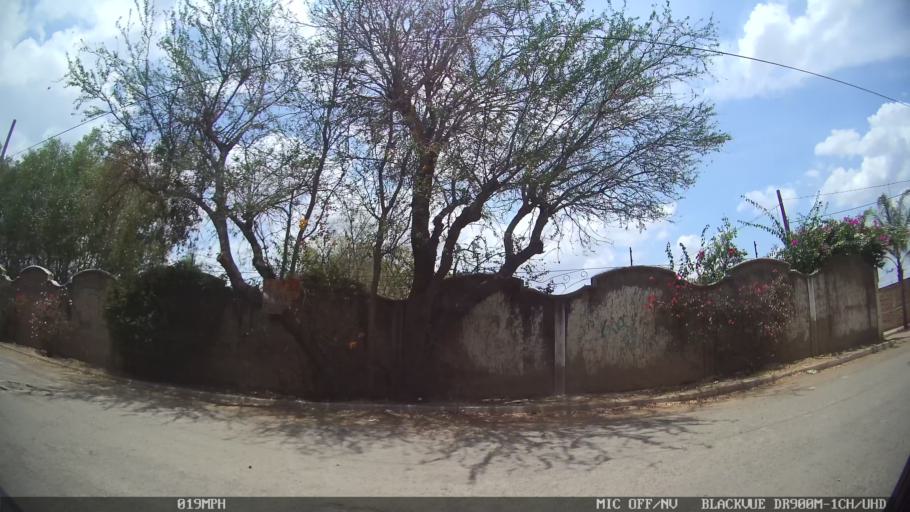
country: MX
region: Jalisco
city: Tonala
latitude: 20.6388
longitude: -103.2218
